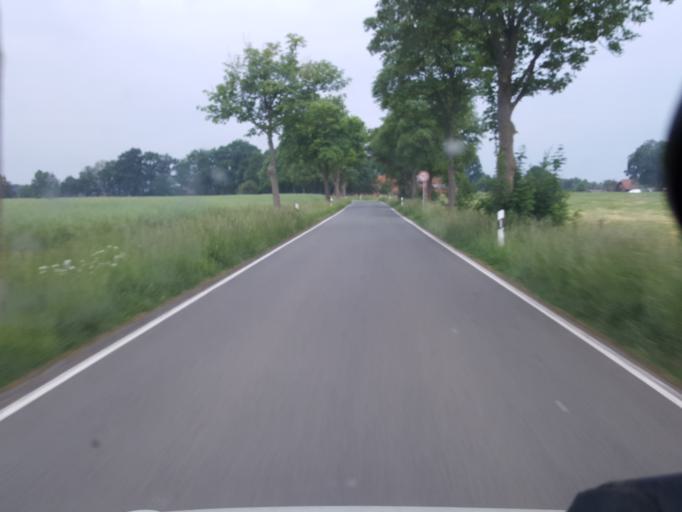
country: DE
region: North Rhine-Westphalia
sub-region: Regierungsbezirk Detmold
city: Minden
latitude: 52.3607
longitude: 8.8571
